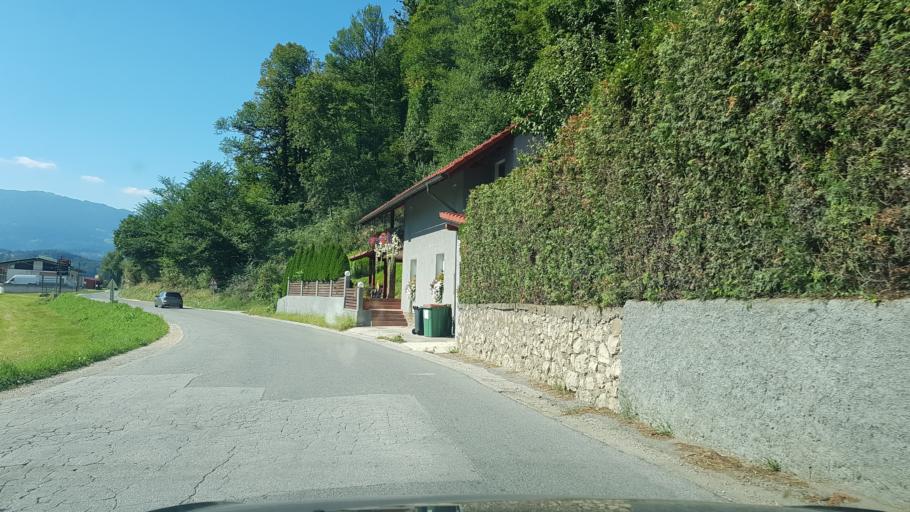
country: SI
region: Smartno ob Paki
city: Smartno ob Paki
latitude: 46.3326
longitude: 15.0347
